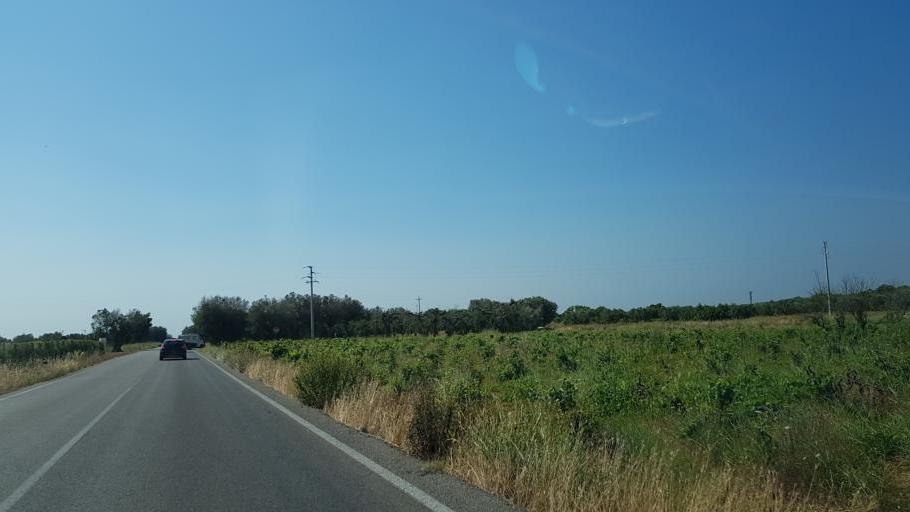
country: IT
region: Apulia
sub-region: Provincia di Lecce
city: Guagnano
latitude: 40.4066
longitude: 17.9653
